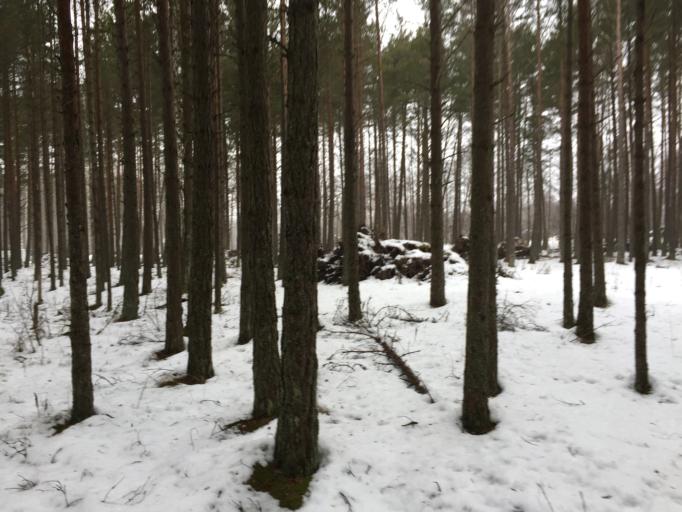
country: EE
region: Saare
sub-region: Kuressaare linn
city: Kuressaare
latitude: 58.2202
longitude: 22.3511
